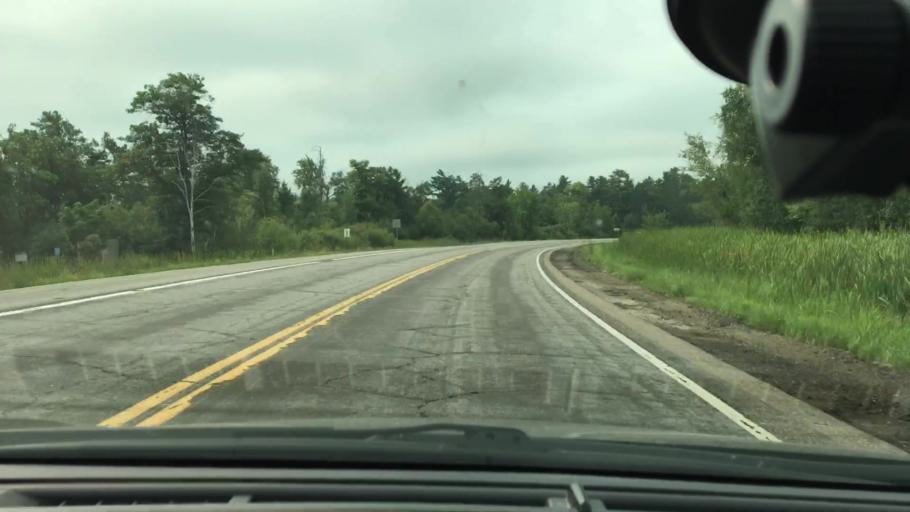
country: US
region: Minnesota
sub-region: Crow Wing County
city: Cross Lake
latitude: 46.7172
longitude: -93.9540
